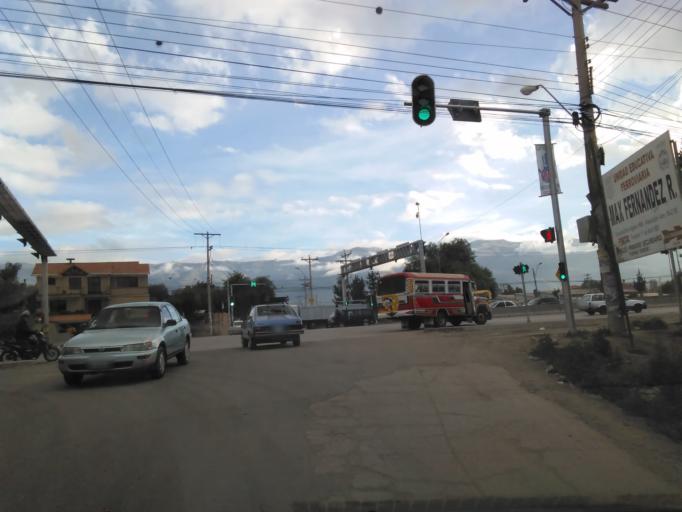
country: BO
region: Cochabamba
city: Cochabamba
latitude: -17.3916
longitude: -66.2300
